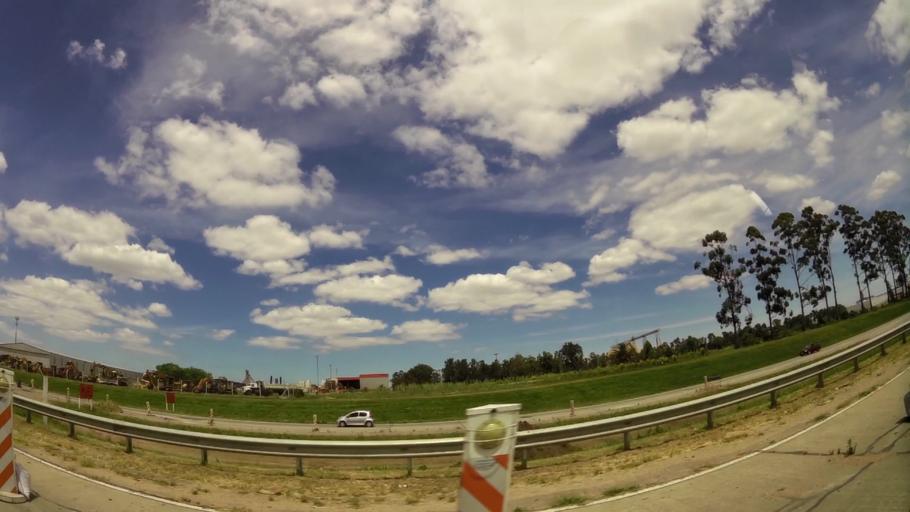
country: UY
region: Montevideo
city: Pajas Blancas
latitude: -34.8534
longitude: -56.2791
